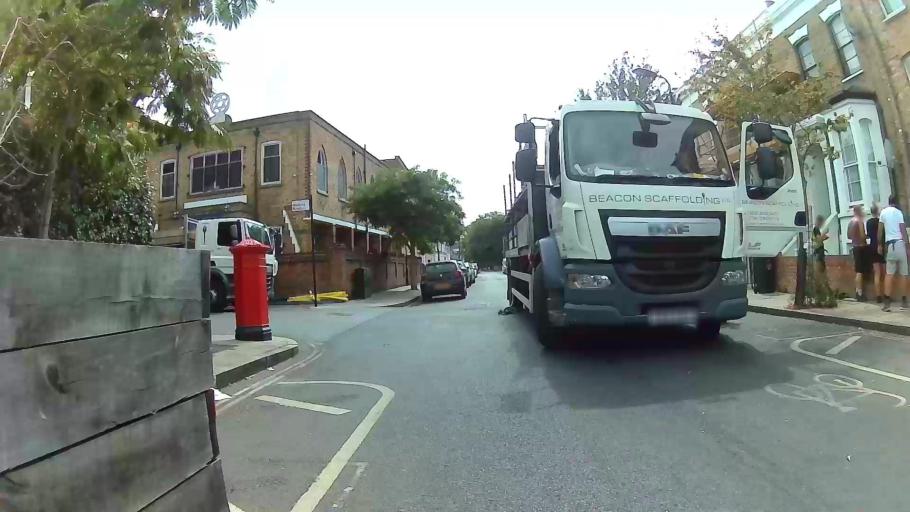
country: GB
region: England
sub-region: Greater London
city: Hackney
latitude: 51.5562
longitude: -0.0790
